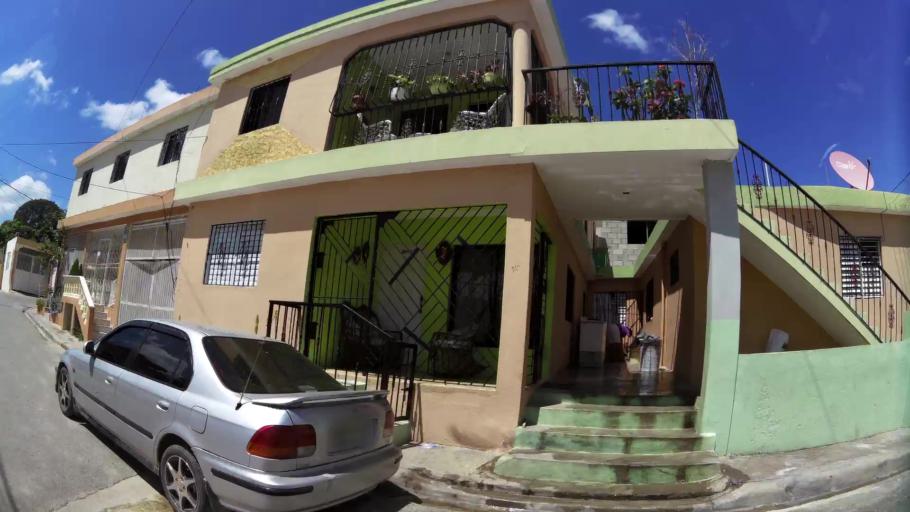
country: DO
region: San Cristobal
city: San Cristobal
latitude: 18.3997
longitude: -70.1114
